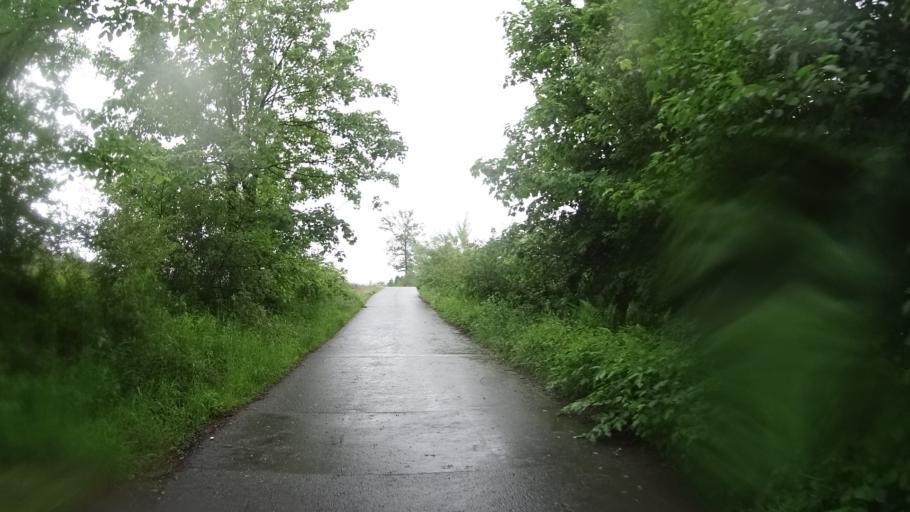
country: CH
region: Saint Gallen
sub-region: Wahlkreis Rheintal
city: Ruthi
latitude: 47.2943
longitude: 9.5564
